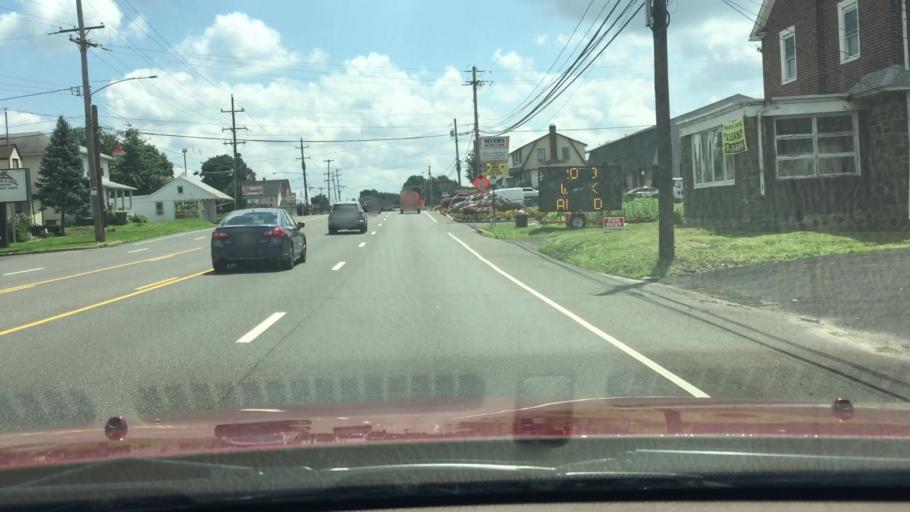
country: US
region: Pennsylvania
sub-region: Montgomery County
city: Horsham
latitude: 40.1745
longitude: -75.1282
